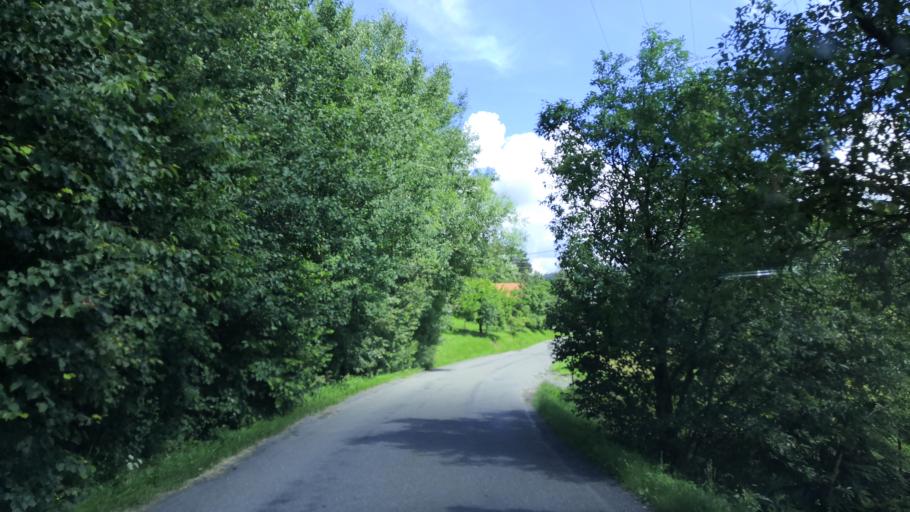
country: CZ
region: Zlin
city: Valasska Bystrice
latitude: 49.4279
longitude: 18.1122
